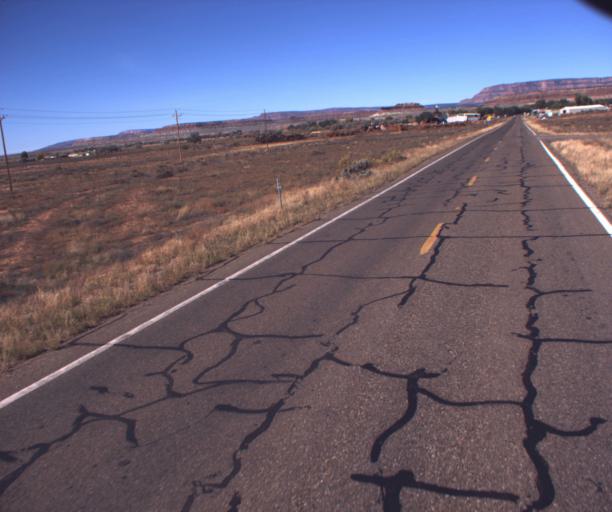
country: US
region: Arizona
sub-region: Coconino County
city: Fredonia
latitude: 36.9374
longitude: -112.5145
